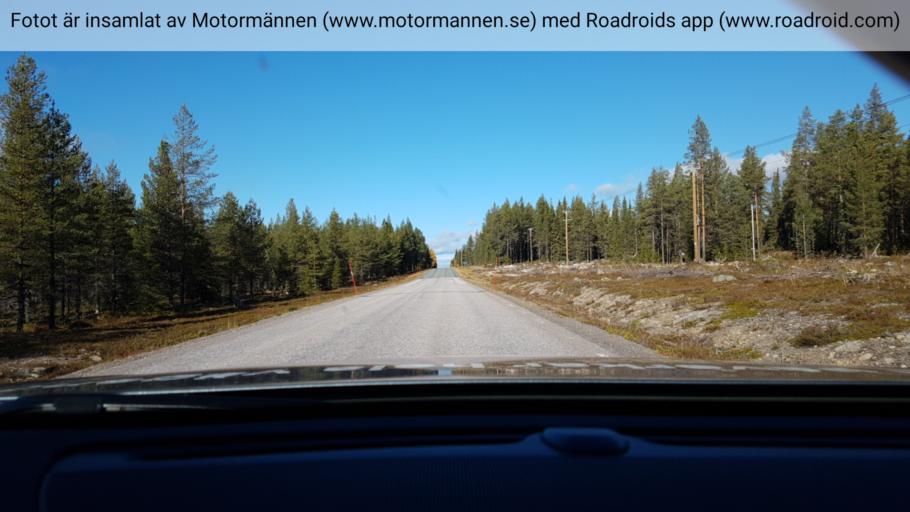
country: SE
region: Vaesterbotten
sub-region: Mala Kommun
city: Mala
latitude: 65.7841
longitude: 18.4975
